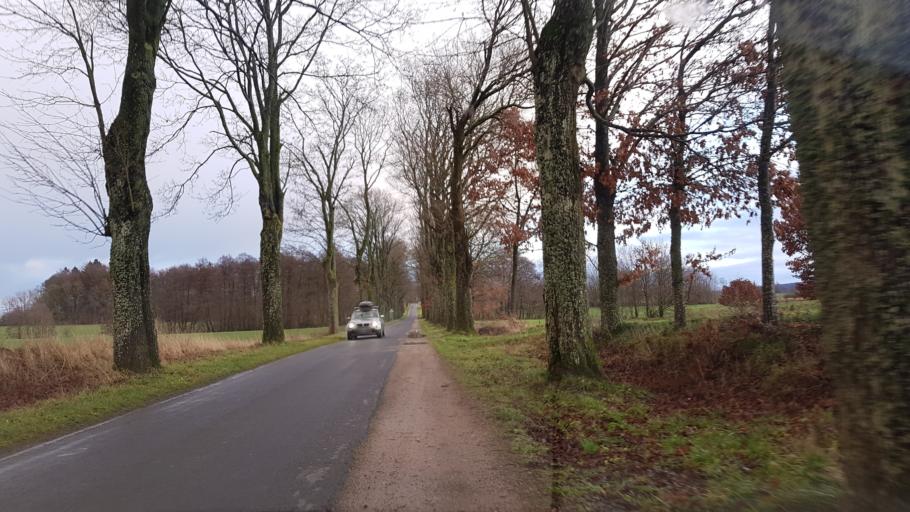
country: PL
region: West Pomeranian Voivodeship
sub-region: Powiat swidwinski
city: Rabino
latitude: 53.9487
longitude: 15.9115
